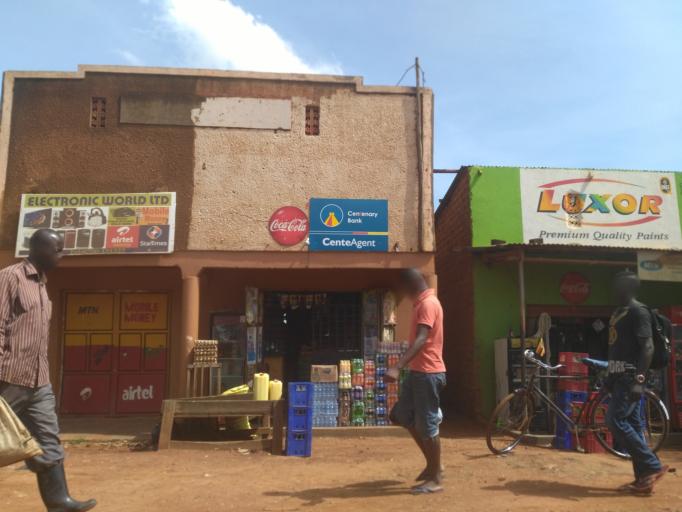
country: UG
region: Central Region
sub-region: Wakiso District
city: Kireka
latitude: 0.4390
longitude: 32.6014
